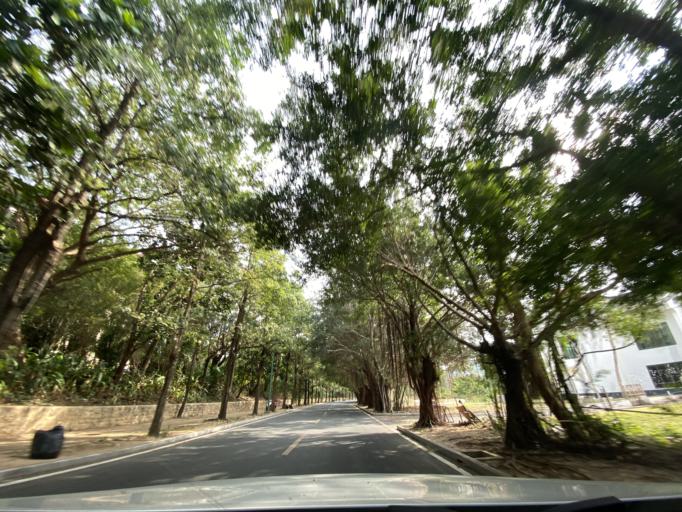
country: CN
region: Hainan
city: Tiandu
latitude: 18.2252
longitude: 109.6206
